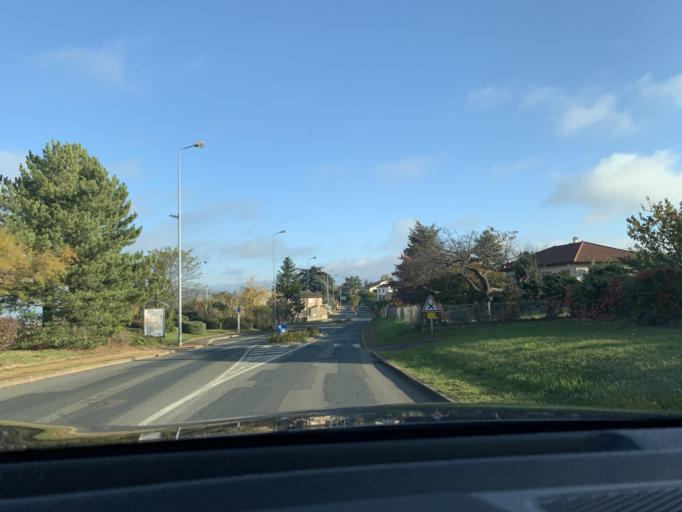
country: FR
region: Rhone-Alpes
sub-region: Departement du Rhone
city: Pommiers
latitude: 45.9502
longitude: 4.6923
